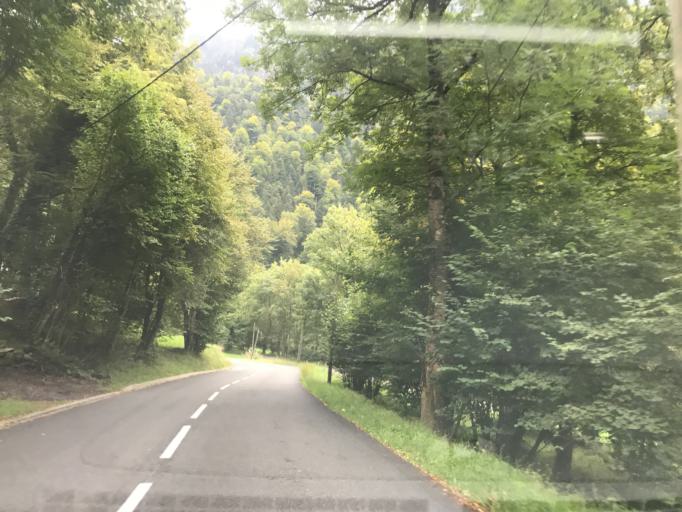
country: FR
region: Midi-Pyrenees
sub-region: Departement de la Haute-Garonne
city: Bagneres-de-Luchon
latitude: 42.7692
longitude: 0.6416
